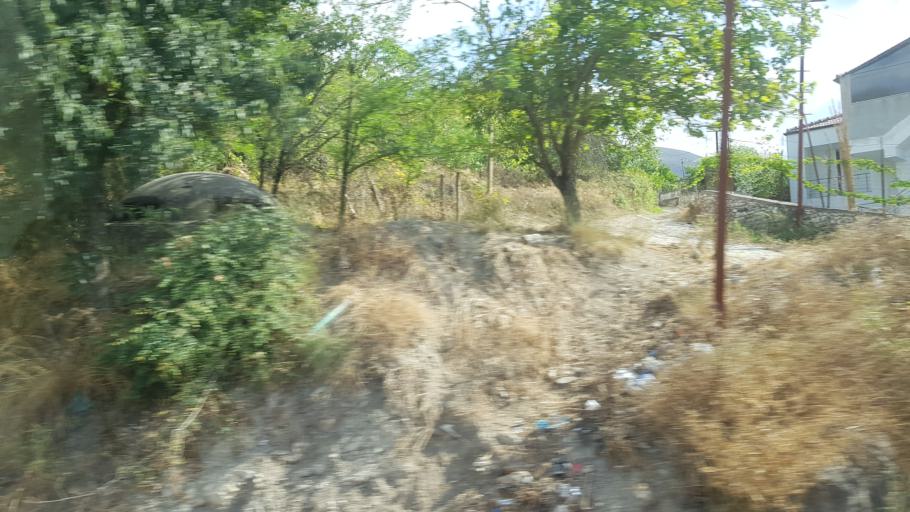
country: AL
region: Vlore
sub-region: Rrethi i Delvines
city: Mesopotam
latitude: 39.9092
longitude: 20.0929
